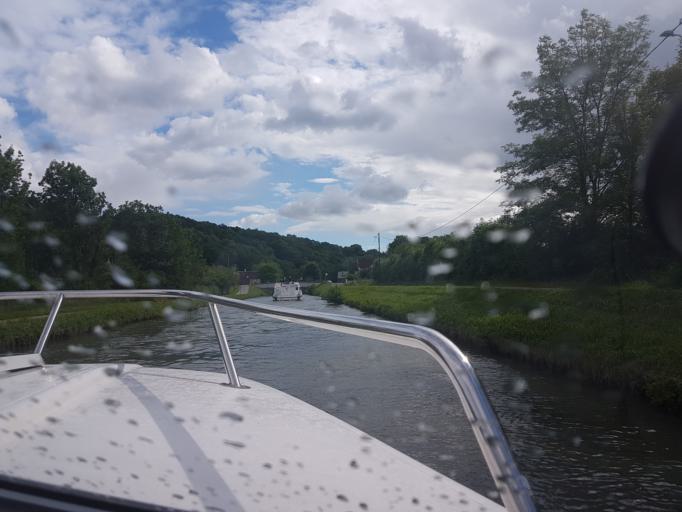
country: FR
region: Bourgogne
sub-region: Departement de la Nievre
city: Clamecy
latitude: 47.5347
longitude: 3.6323
